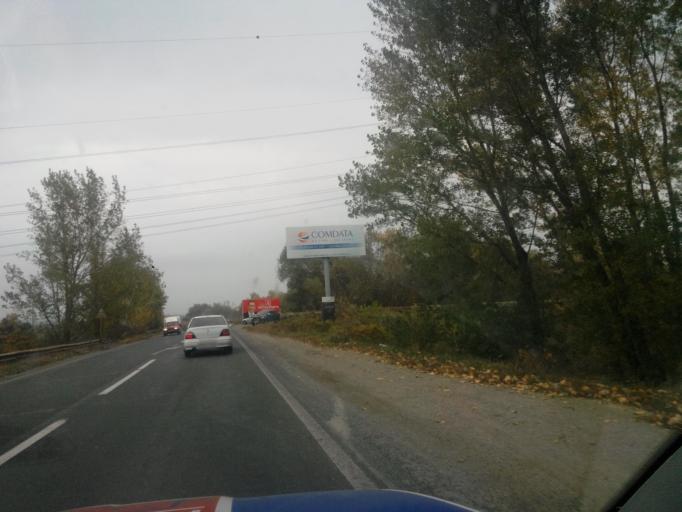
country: RO
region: Galati
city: Galati
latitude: 45.3786
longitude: 28.0182
